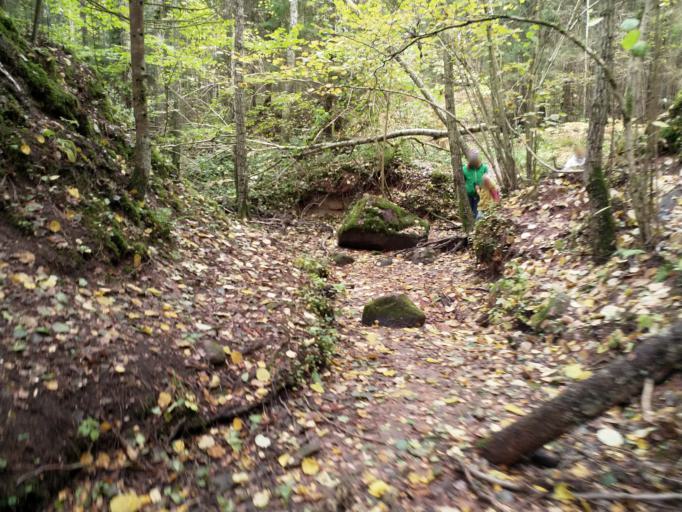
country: LV
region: Dundaga
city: Dundaga
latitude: 57.6544
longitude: 22.2826
